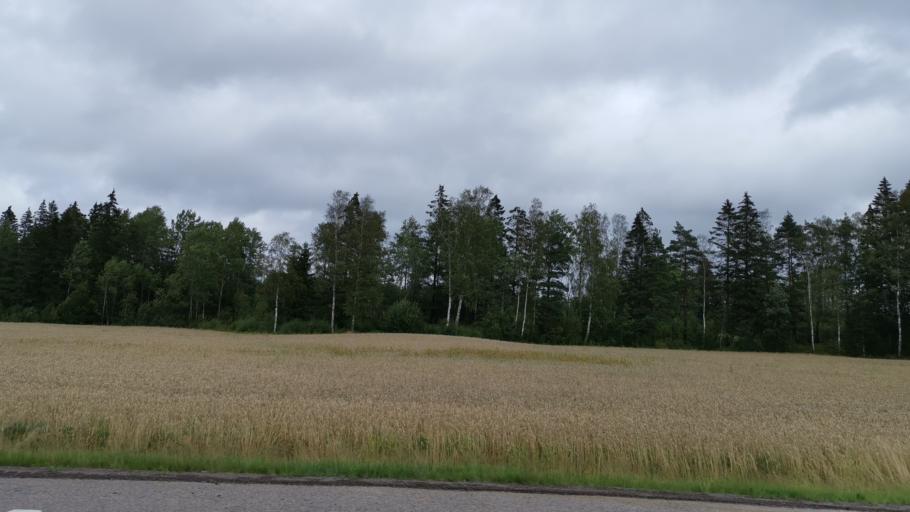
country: SE
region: Vaestra Goetaland
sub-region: Trollhattan
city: Sjuntorp
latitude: 58.3386
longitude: 12.1221
